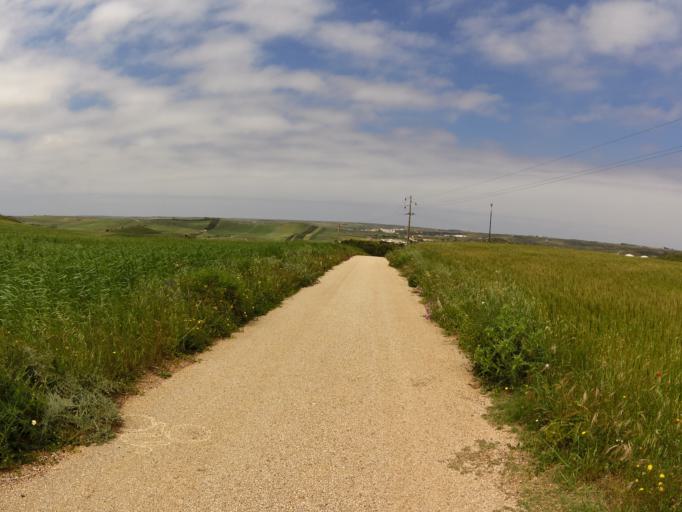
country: PT
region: Faro
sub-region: Vila do Bispo
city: Vila do Bispo
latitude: 37.0799
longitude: -8.8808
